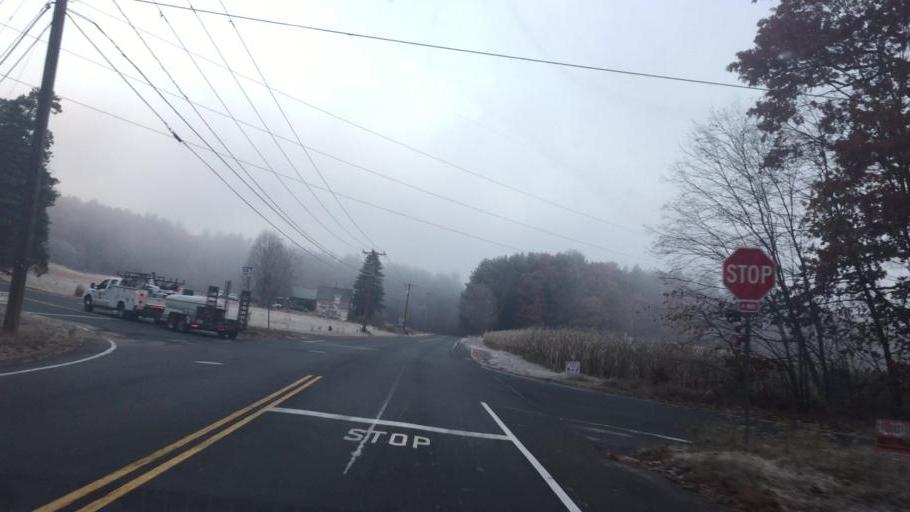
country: US
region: Massachusetts
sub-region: Hampshire County
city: Southampton
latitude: 42.2129
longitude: -72.6904
